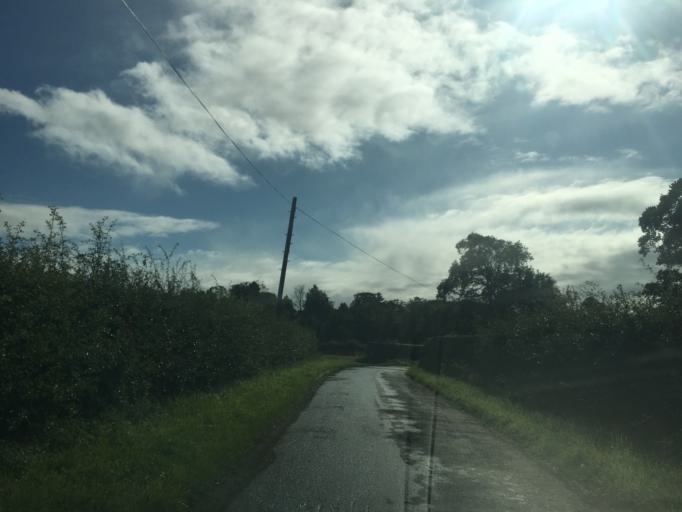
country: GB
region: Scotland
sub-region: Edinburgh
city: Kirkliston
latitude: 55.9586
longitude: -3.3743
